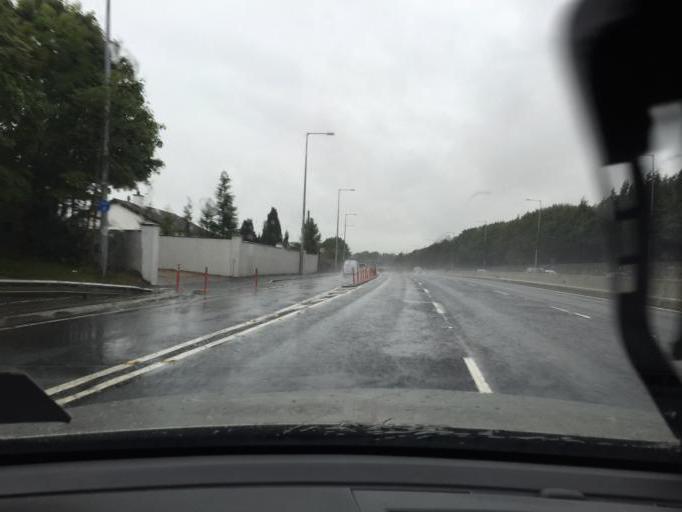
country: IE
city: Palmerstown
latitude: 53.3587
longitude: -6.4119
